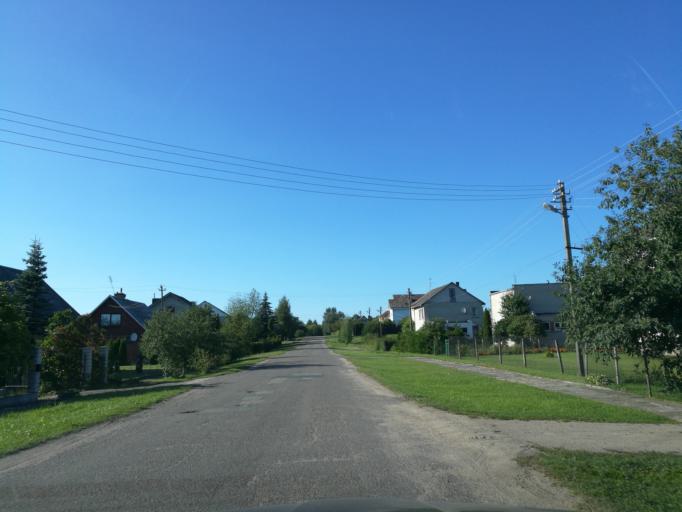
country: LT
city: Trakai
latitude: 54.6064
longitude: 24.9770
